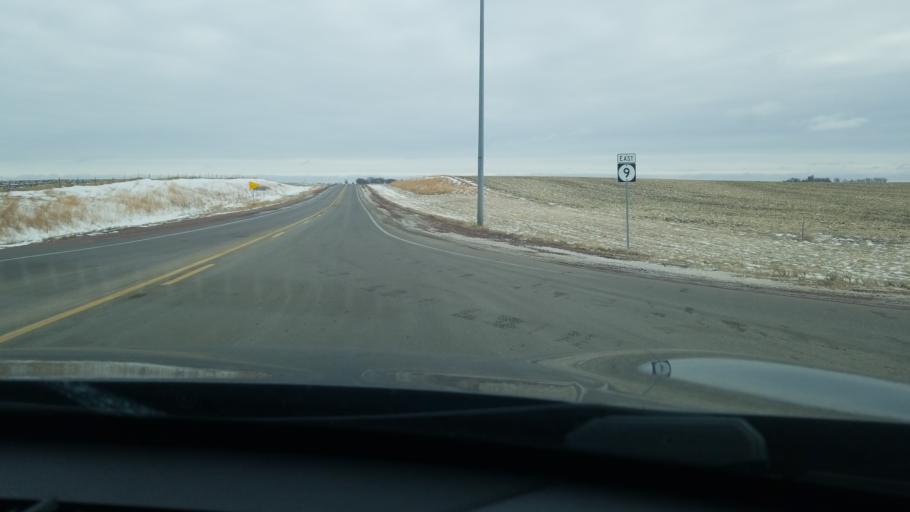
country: US
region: South Dakota
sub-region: Lincoln County
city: Canton
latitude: 43.4331
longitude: -96.4289
